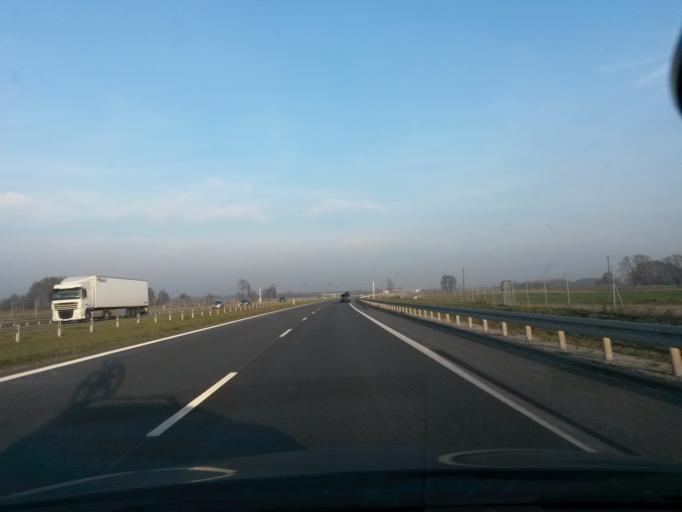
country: PL
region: Greater Poland Voivodeship
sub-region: Powiat kepinski
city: Bralin
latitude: 51.3088
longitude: 17.9273
